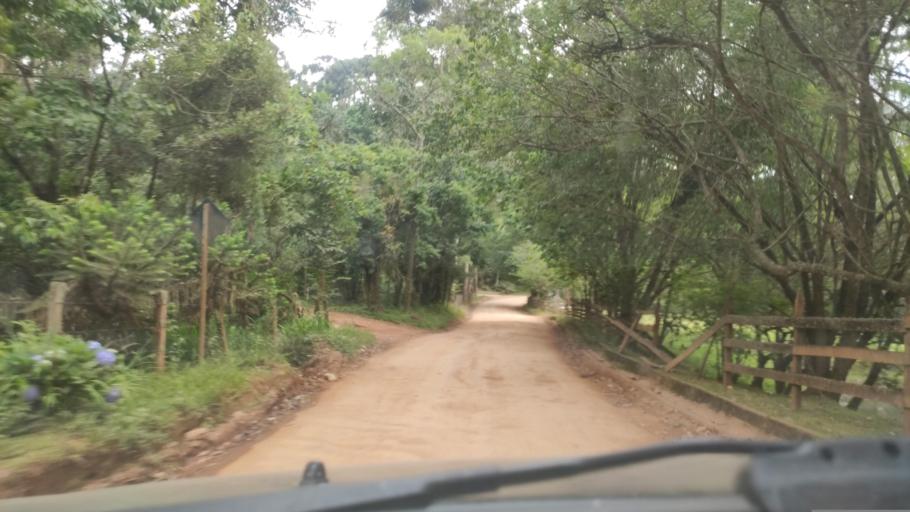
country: BR
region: Minas Gerais
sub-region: Paraisopolis
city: Paraisopolis
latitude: -22.6851
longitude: -45.8558
